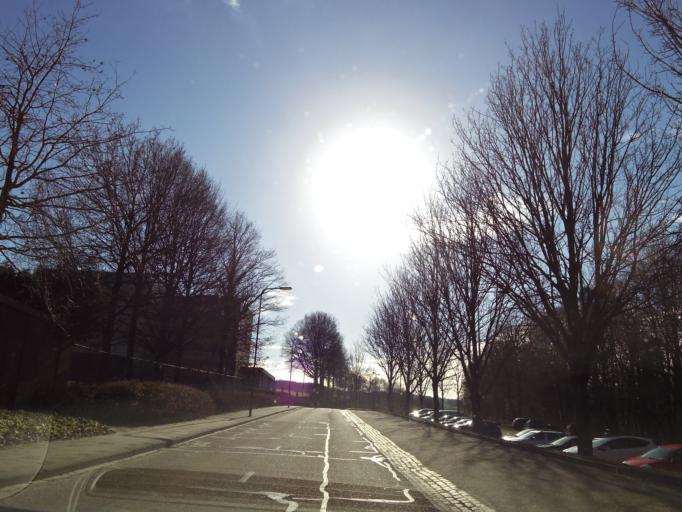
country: NL
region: Limburg
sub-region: Valkenburg aan de Geul
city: Schin op Geul
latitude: 50.8100
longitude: 5.8887
